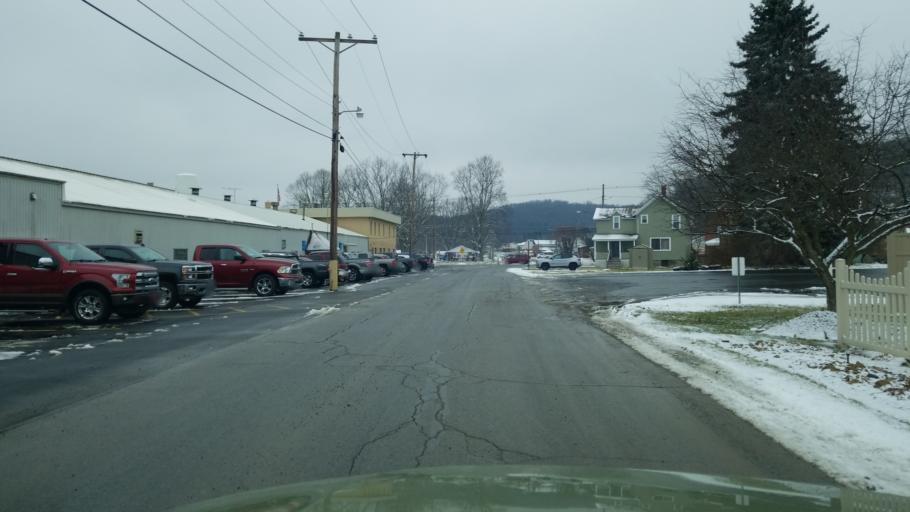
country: US
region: Pennsylvania
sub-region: Jefferson County
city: Sykesville
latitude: 41.0498
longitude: -78.8208
